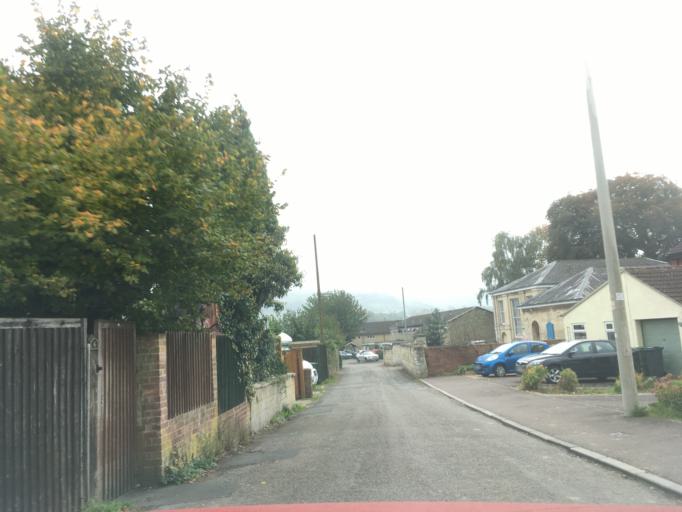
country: GB
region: England
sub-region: Gloucestershire
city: Stonehouse
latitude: 51.7433
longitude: -2.2519
